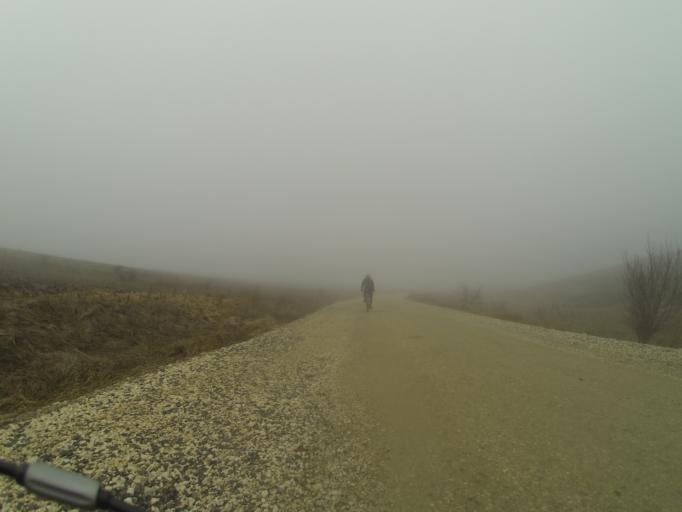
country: RO
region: Mehedinti
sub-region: Comuna Balacita
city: Gvardinita
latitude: 44.4247
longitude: 23.1302
